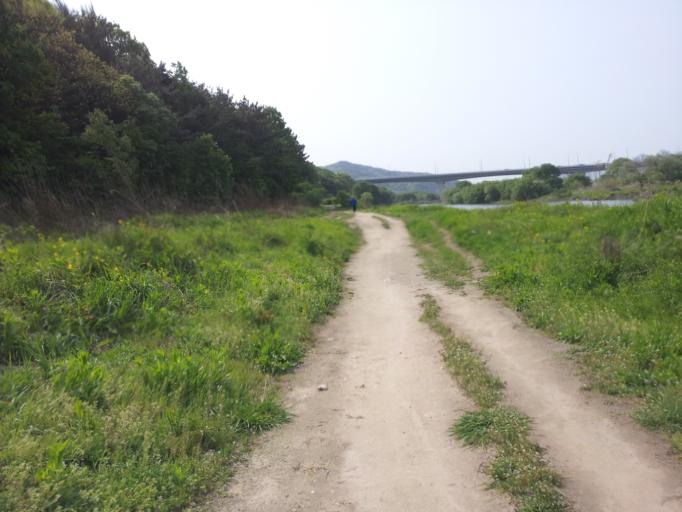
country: KR
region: Daejeon
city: Daejeon
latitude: 36.3360
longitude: 127.3546
